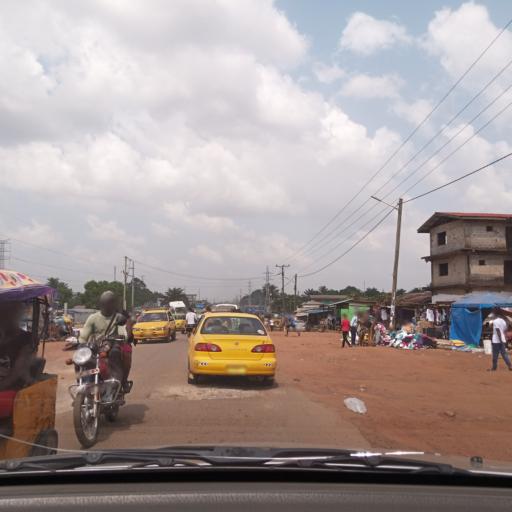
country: LR
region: Montserrado
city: Monrovia
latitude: 6.2802
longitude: -10.6920
